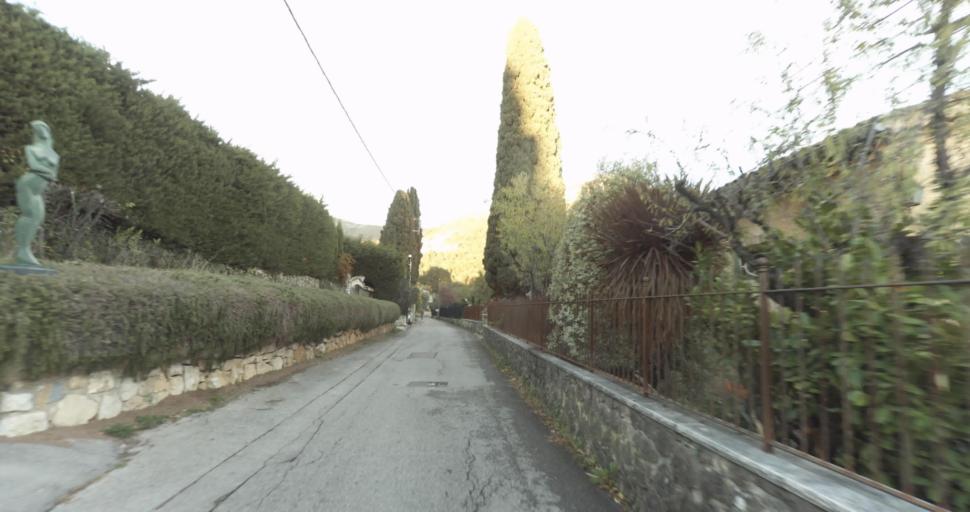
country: FR
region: Provence-Alpes-Cote d'Azur
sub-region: Departement des Alpes-Maritimes
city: Vence
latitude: 43.7296
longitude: 7.1006
